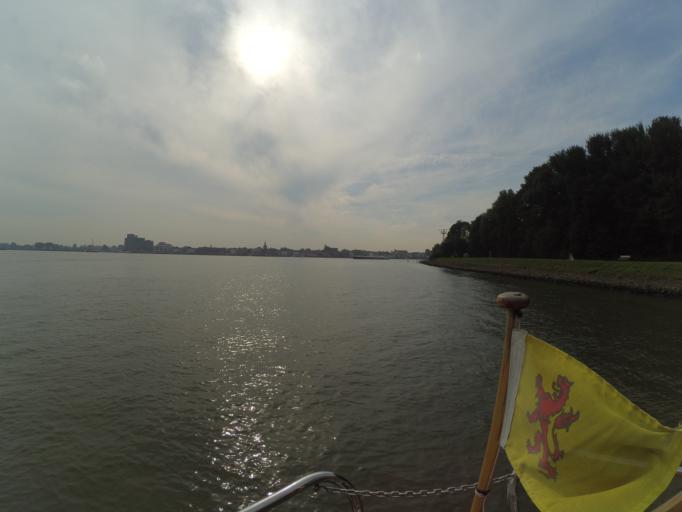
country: NL
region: South Holland
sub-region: Gemeente Dordrecht
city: Dordrecht
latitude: 51.8251
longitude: 4.6682
